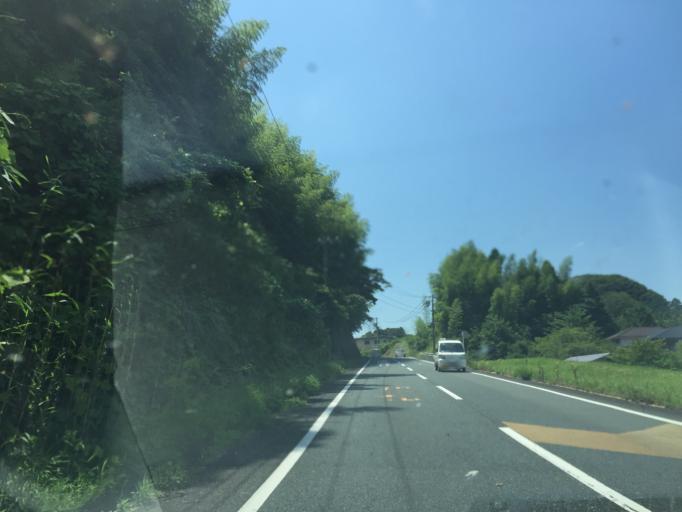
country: JP
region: Shizuoka
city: Kakegawa
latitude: 34.7977
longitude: 137.9860
